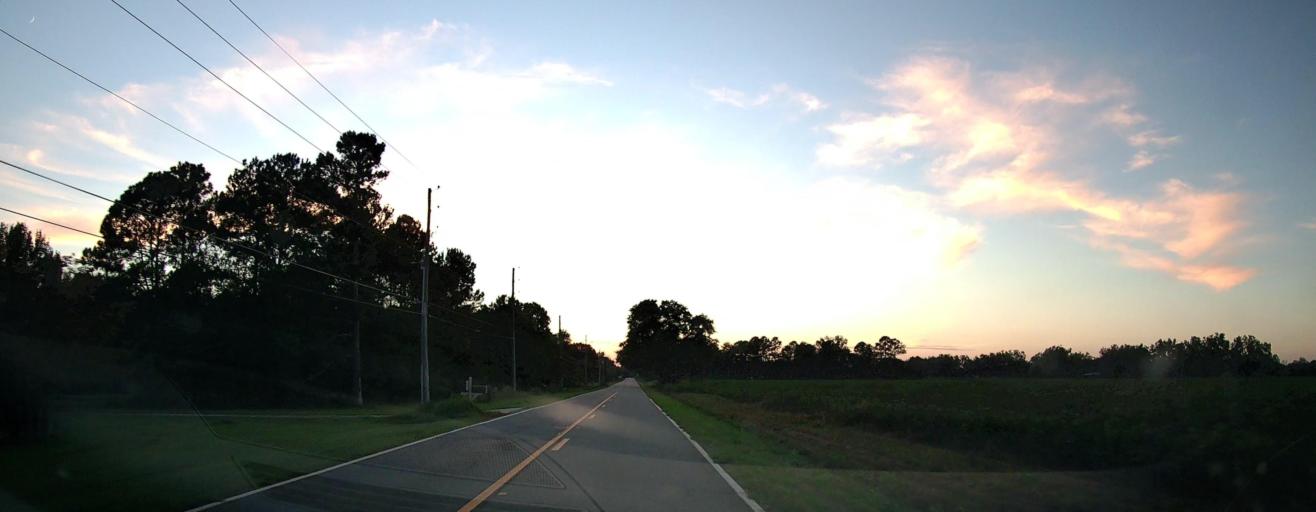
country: US
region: Georgia
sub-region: Houston County
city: Centerville
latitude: 32.6433
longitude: -83.7019
